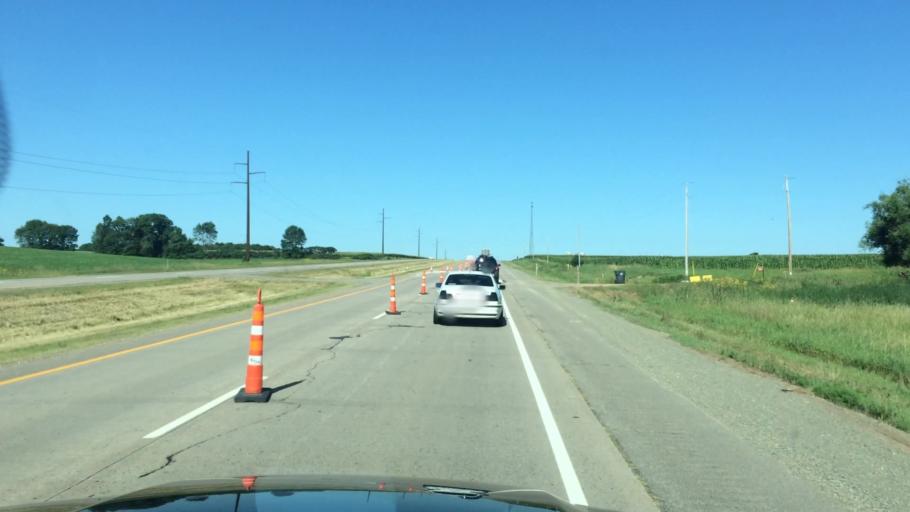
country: US
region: Wisconsin
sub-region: Marathon County
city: Marathon
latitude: 44.9446
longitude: -89.8909
